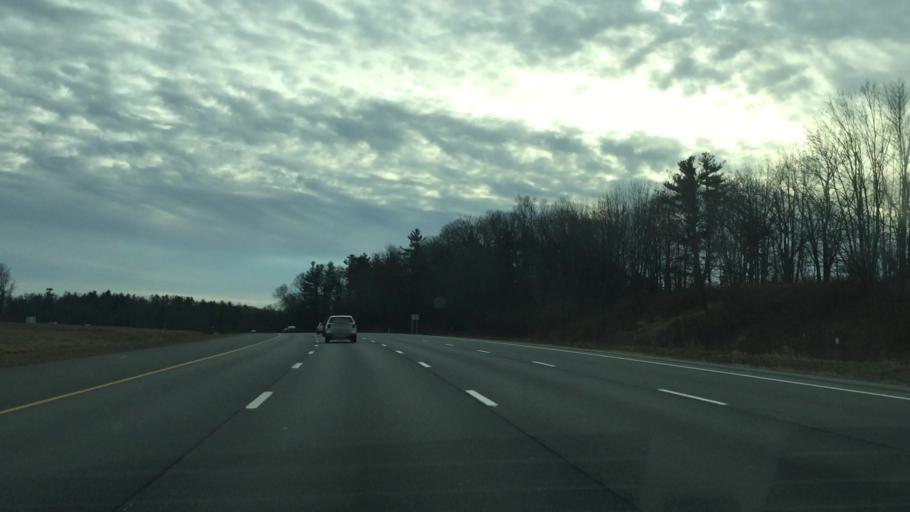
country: US
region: New Hampshire
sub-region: Rockingham County
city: Windham
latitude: 42.7958
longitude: -71.2724
